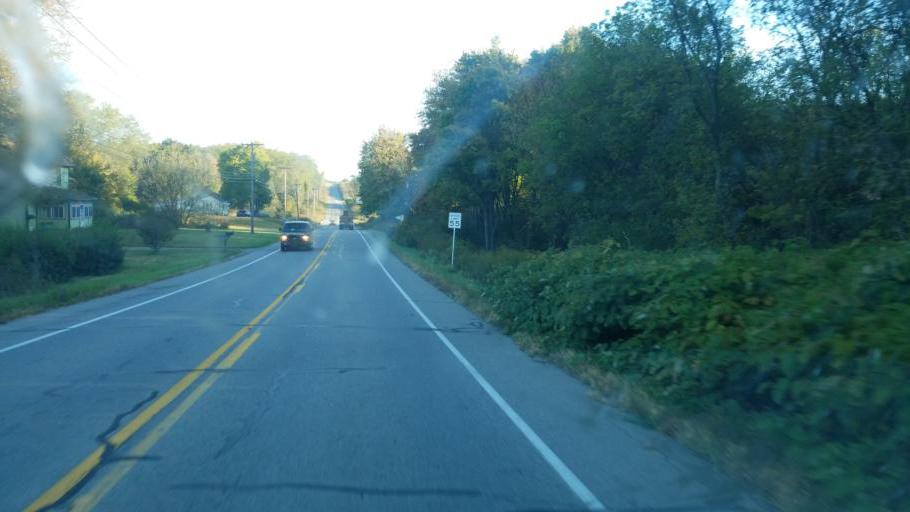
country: US
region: Pennsylvania
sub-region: Mercer County
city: Mercer
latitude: 41.2002
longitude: -80.2408
